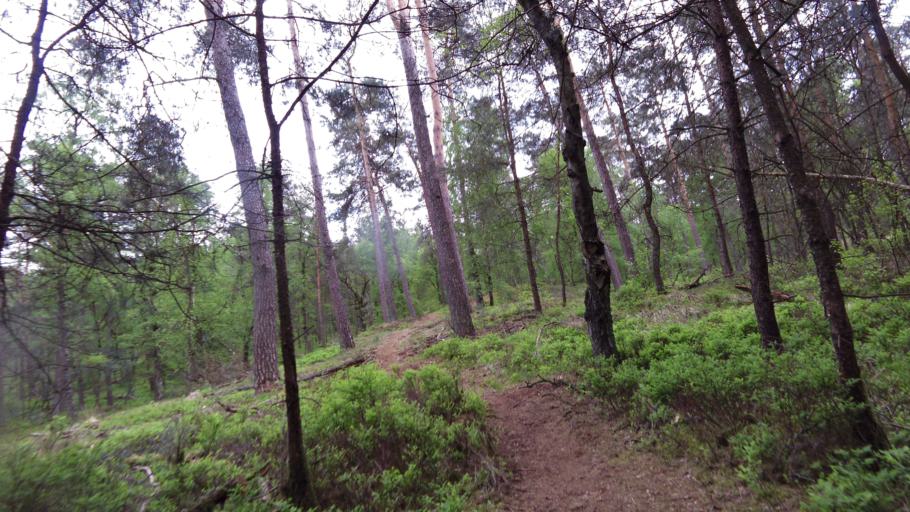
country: NL
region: Gelderland
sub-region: Gemeente Brummen
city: Eerbeek
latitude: 52.0679
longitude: 6.0481
